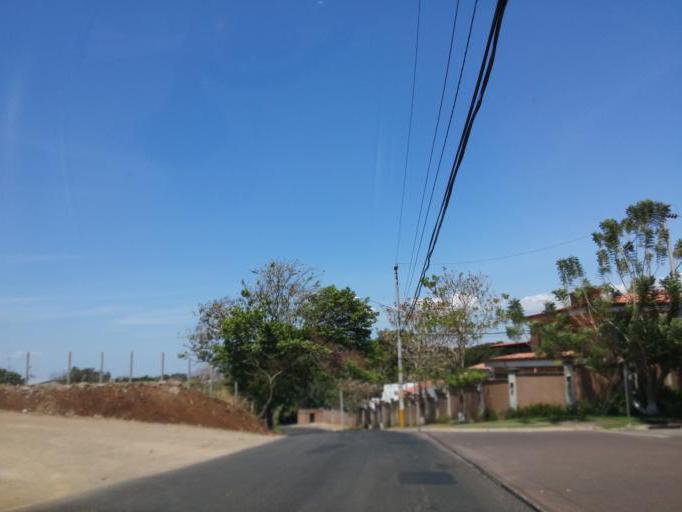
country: CR
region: Alajuela
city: Alajuela
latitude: 10.0165
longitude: -84.2270
